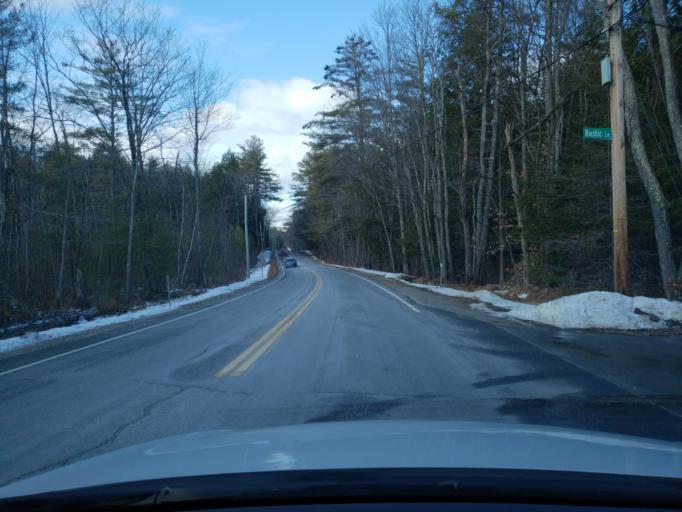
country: US
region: New Hampshire
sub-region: Hillsborough County
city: New Boston
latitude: 42.9927
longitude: -71.7435
